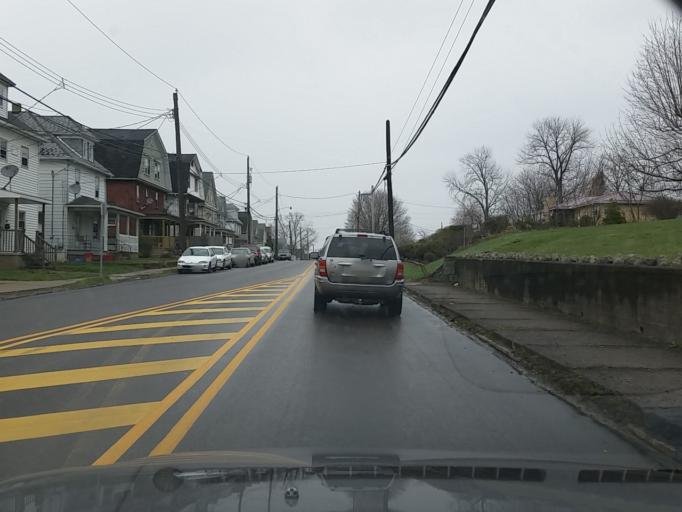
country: US
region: Pennsylvania
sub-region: Luzerne County
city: Nanticoke
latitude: 41.2061
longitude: -75.9931
